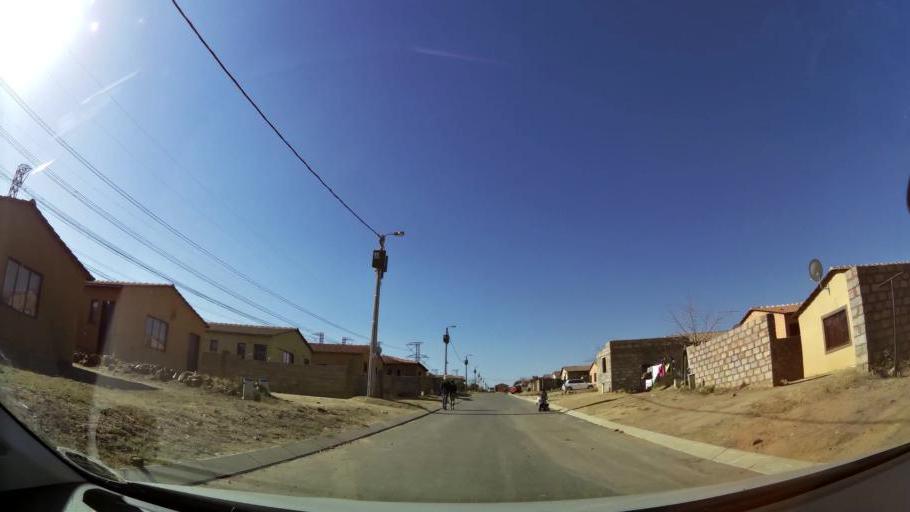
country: ZA
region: Gauteng
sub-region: Ekurhuleni Metropolitan Municipality
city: Tembisa
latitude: -26.0336
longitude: 28.2188
